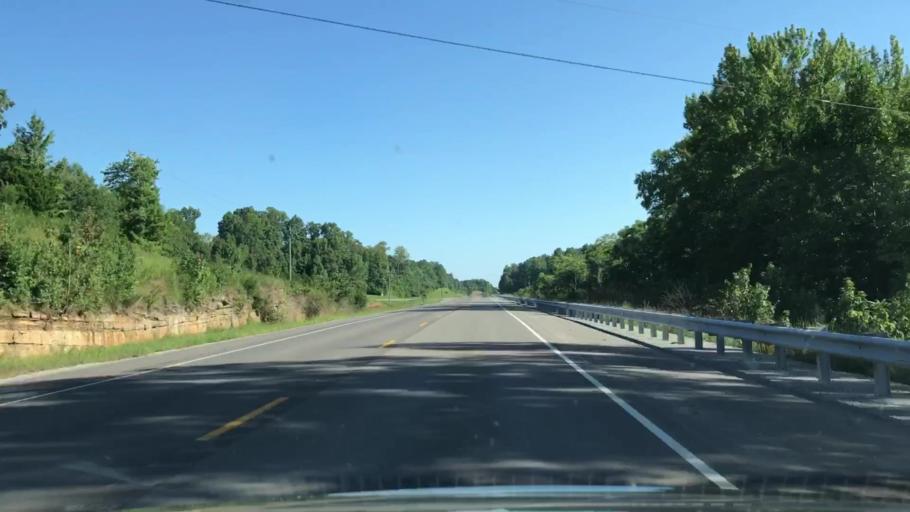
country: US
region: Kentucky
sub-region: Cumberland County
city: Burkesville
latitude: 36.6949
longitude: -85.3733
